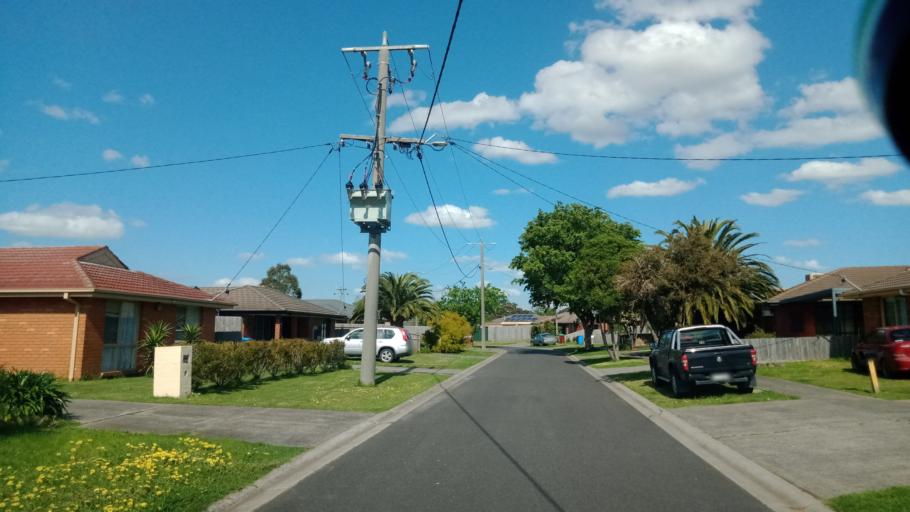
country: AU
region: Victoria
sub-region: Casey
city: Cranbourne West
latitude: -38.1036
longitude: 145.2545
